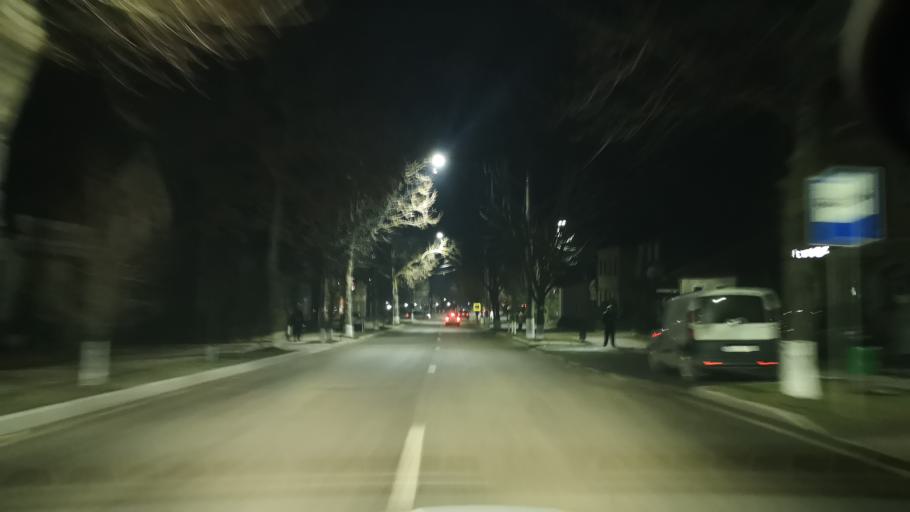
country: MD
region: Orhei
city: Orhei
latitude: 47.3832
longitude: 28.8254
